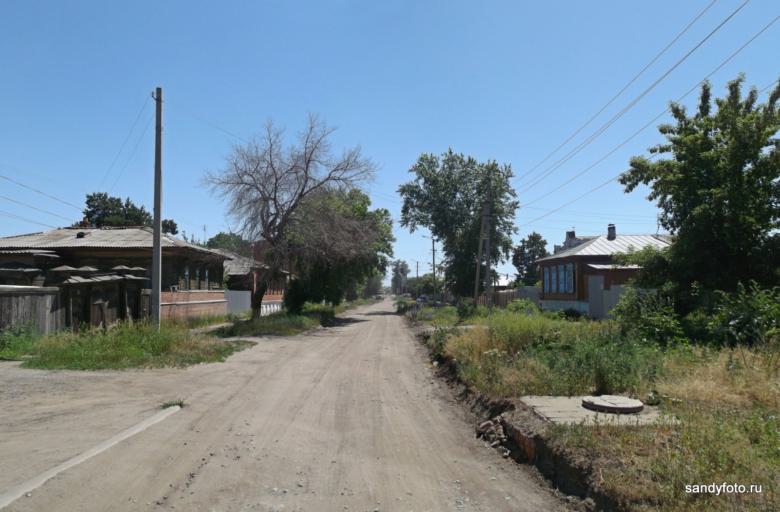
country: RU
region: Chelyabinsk
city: Troitsk
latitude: 54.0793
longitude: 61.5477
